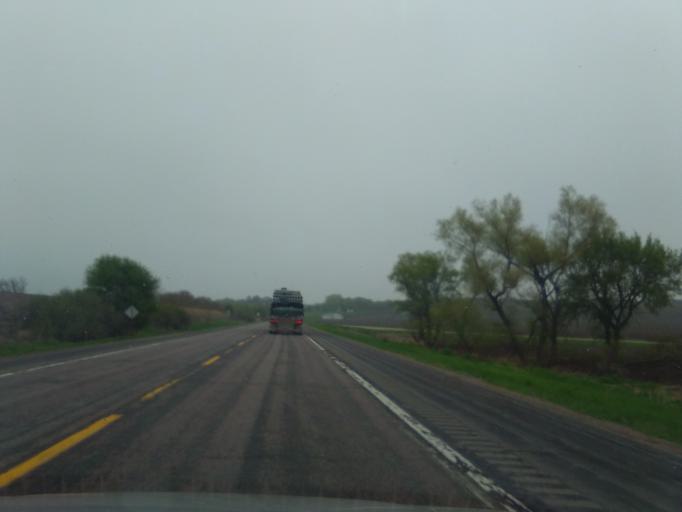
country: US
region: Nebraska
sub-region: Burt County
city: Oakland
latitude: 41.8133
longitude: -96.4744
